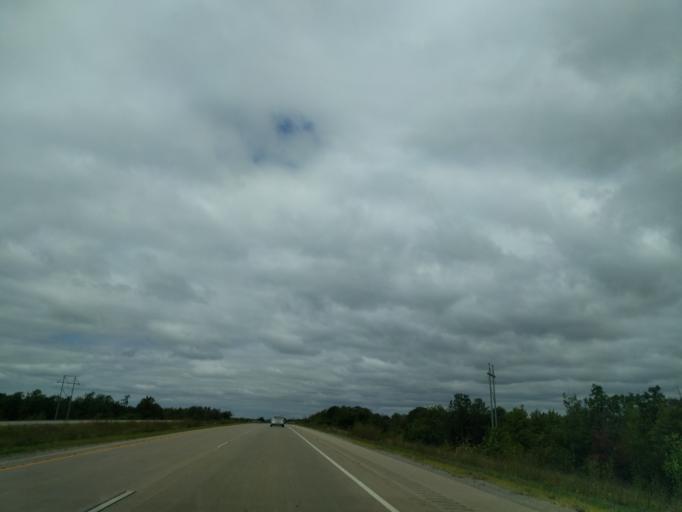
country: US
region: Wisconsin
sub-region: Marinette County
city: Peshtigo
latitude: 45.0418
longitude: -87.7556
